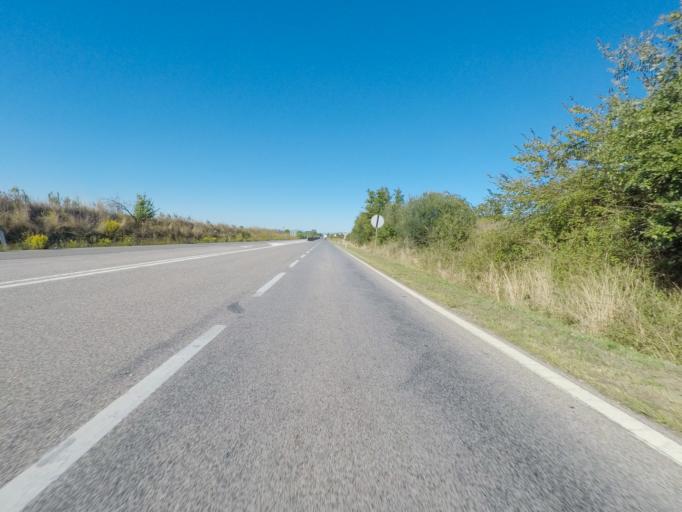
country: IT
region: Tuscany
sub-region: Provincia di Grosseto
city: Grosseto
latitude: 42.6788
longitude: 11.1406
